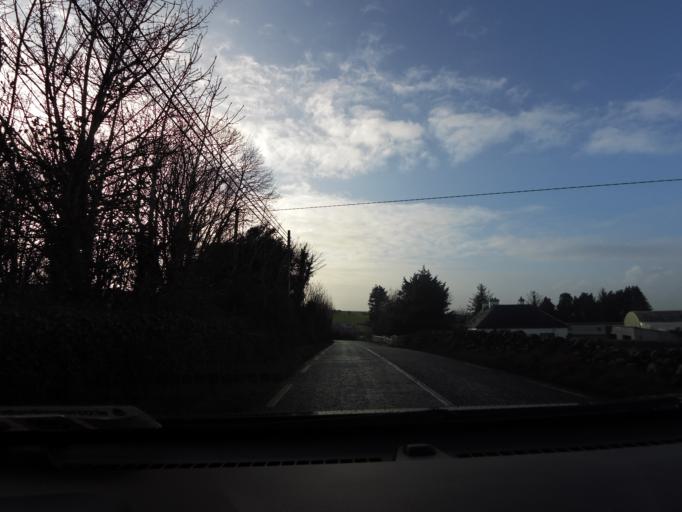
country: IE
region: Connaught
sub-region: County Galway
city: Tuam
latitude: 53.4878
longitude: -8.9982
